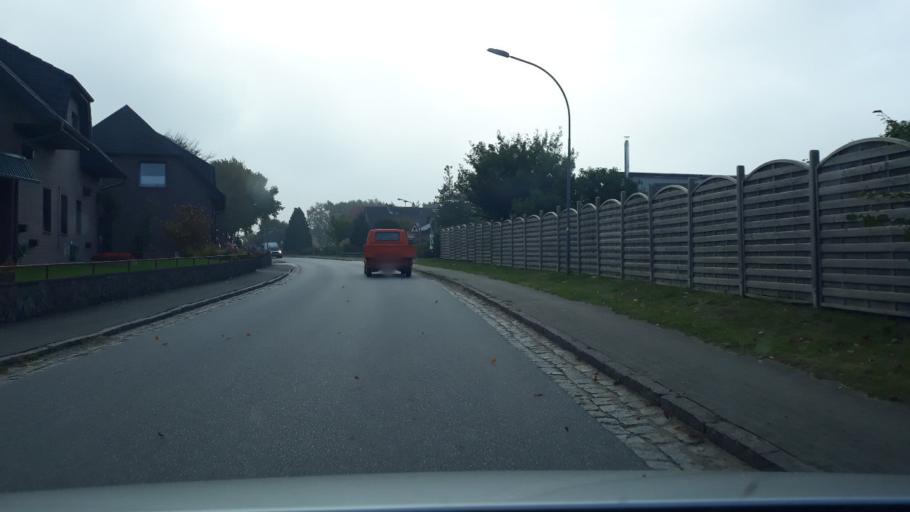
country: DE
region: Schleswig-Holstein
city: Klein Rheide
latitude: 54.4502
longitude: 9.4765
